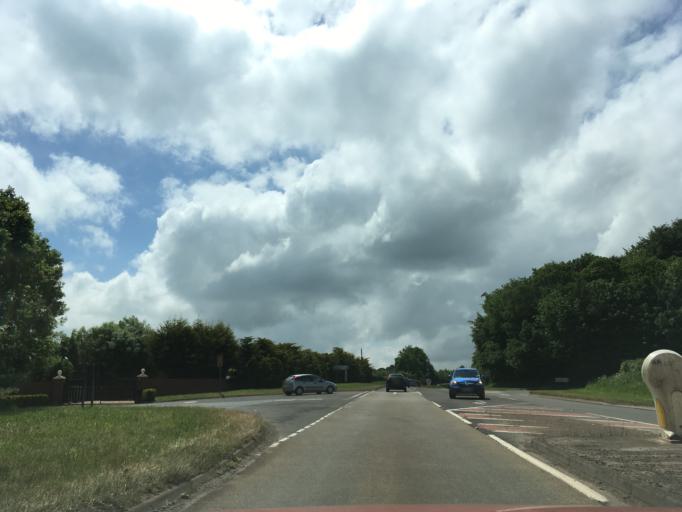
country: GB
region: England
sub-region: Devon
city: Uffculme
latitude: 50.9412
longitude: -3.3013
